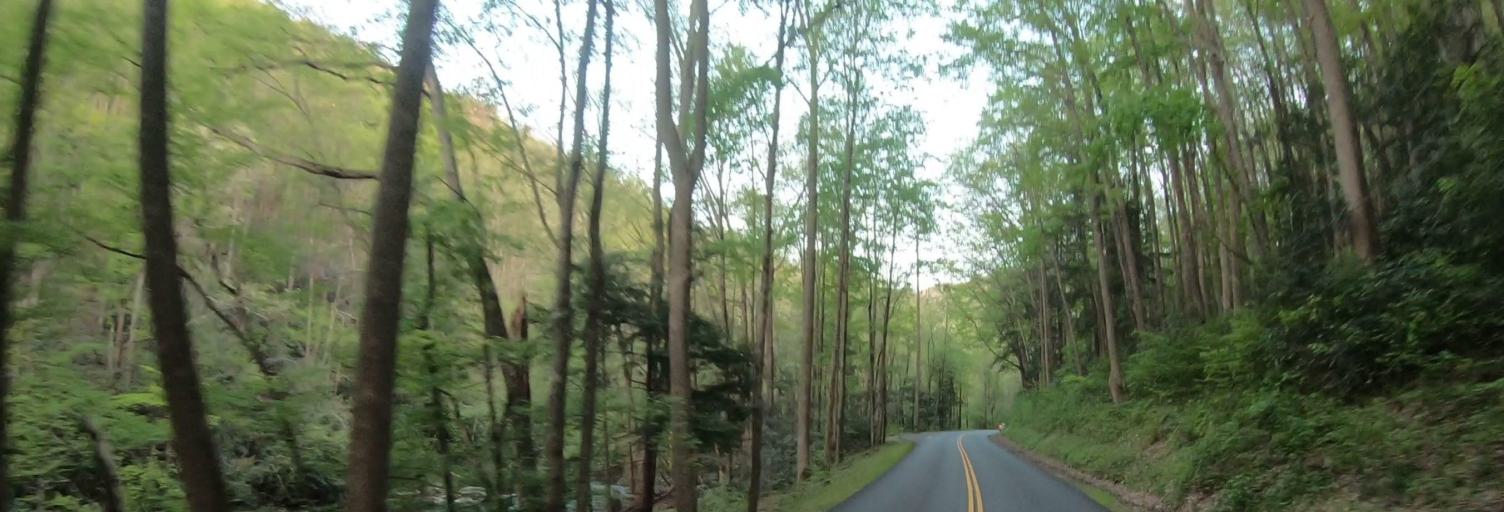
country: US
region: Tennessee
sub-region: Sevier County
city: Gatlinburg
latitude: 35.6701
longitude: -83.6372
